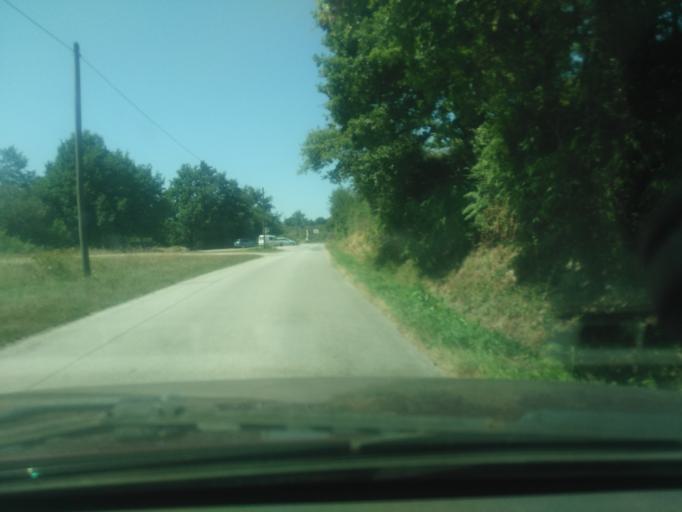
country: FR
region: Pays de la Loire
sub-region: Departement de la Vendee
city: Dompierre-sur-Yon
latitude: 46.7216
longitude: -1.3883
